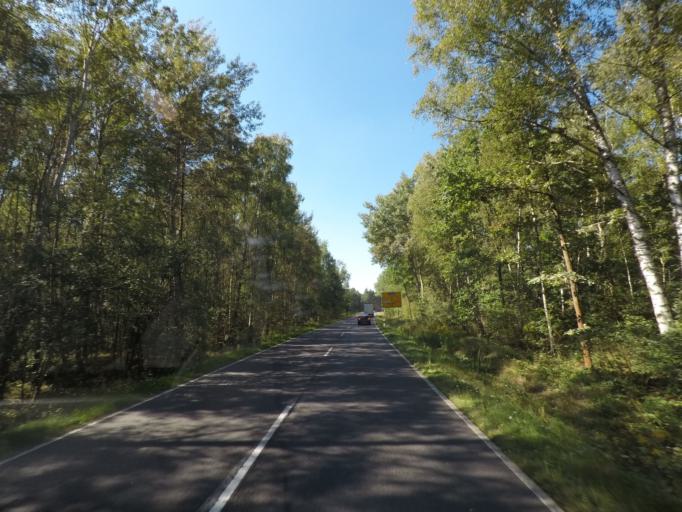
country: DE
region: Brandenburg
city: Welzow
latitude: 51.5635
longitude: 14.1142
